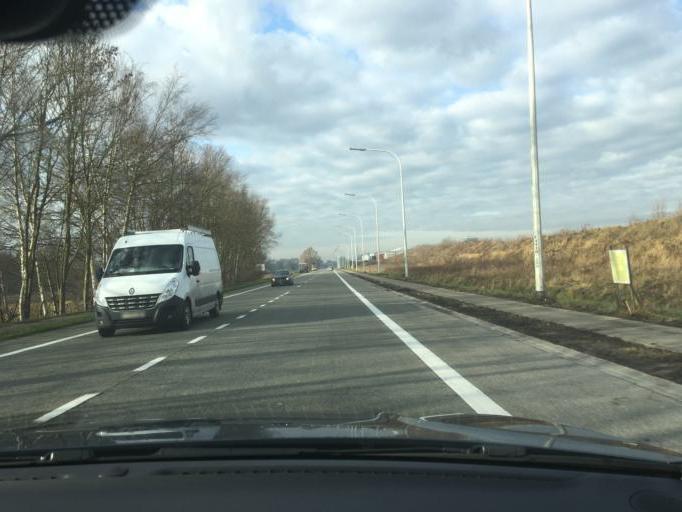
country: BE
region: Wallonia
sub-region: Province du Hainaut
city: Estaimpuis
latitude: 50.7175
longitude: 3.2906
